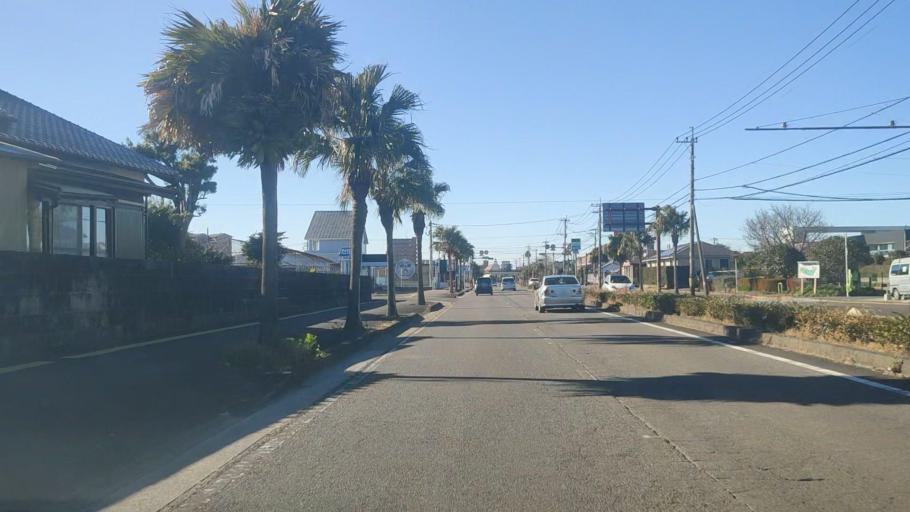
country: JP
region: Miyazaki
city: Miyazaki-shi
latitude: 31.9425
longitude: 131.4391
